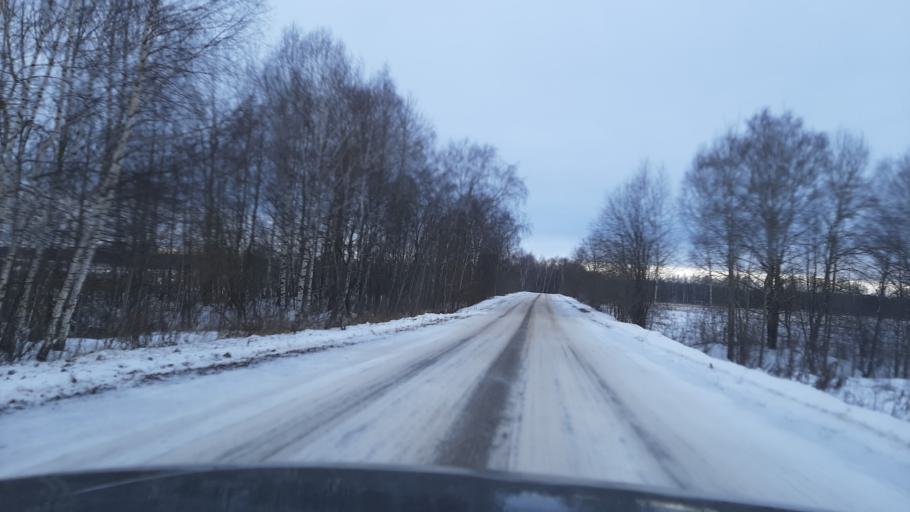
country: RU
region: Kostroma
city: Volgorechensk
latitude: 57.4373
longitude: 41.0514
